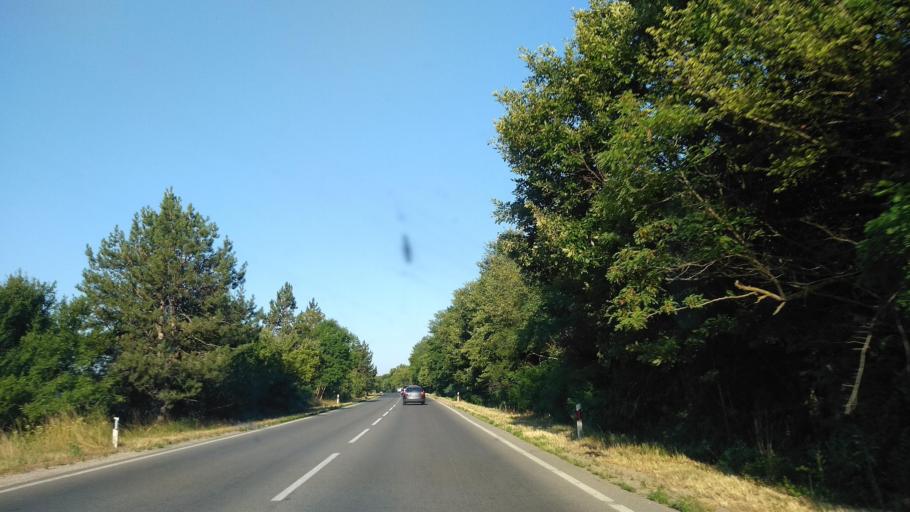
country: BG
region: Gabrovo
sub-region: Obshtina Sevlievo
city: Sevlievo
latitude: 43.0474
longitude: 25.2383
